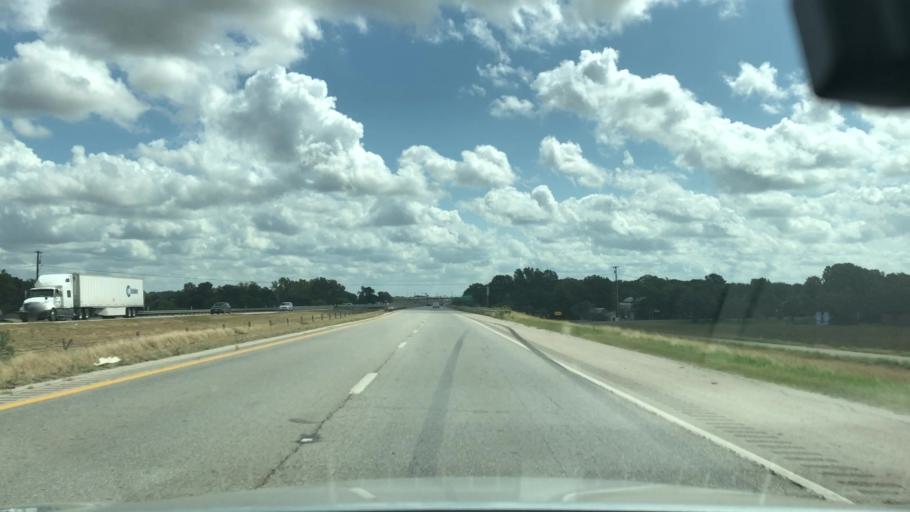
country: US
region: Texas
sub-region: Guadalupe County
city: McQueeney
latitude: 29.5650
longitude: -98.0261
